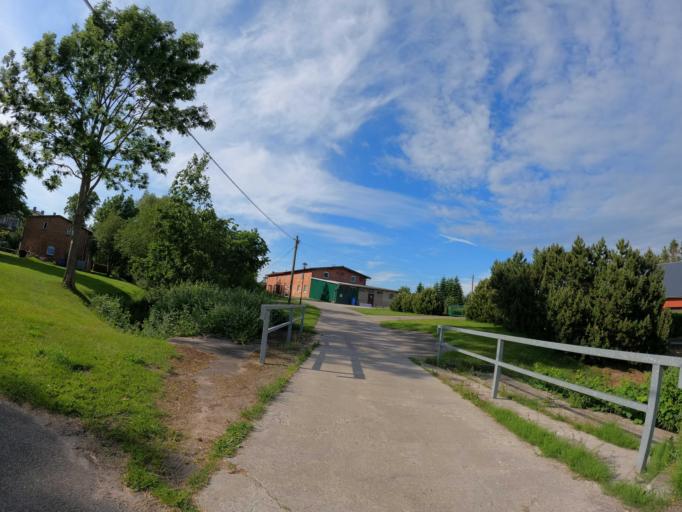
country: DE
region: Mecklenburg-Vorpommern
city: Preetz
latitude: 54.3519
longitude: 12.9905
